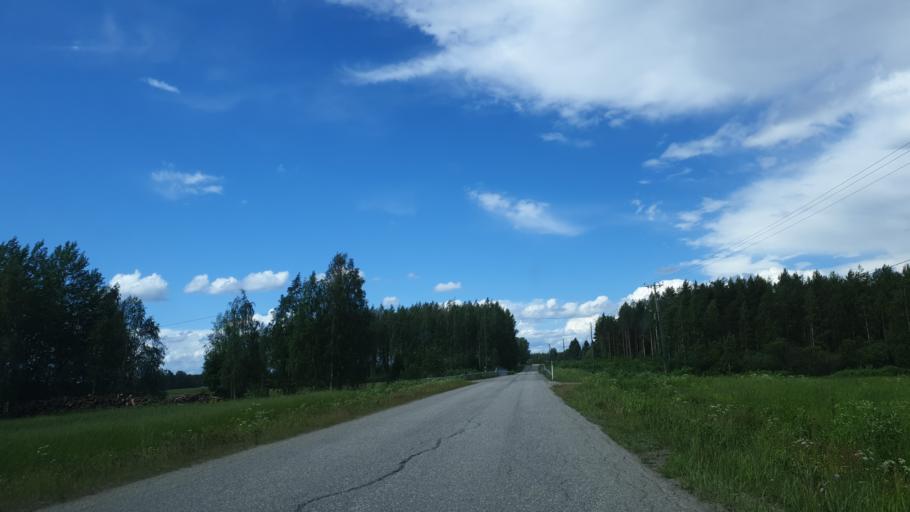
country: FI
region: Northern Savo
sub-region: Koillis-Savo
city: Kaavi
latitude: 62.9854
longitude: 28.7357
